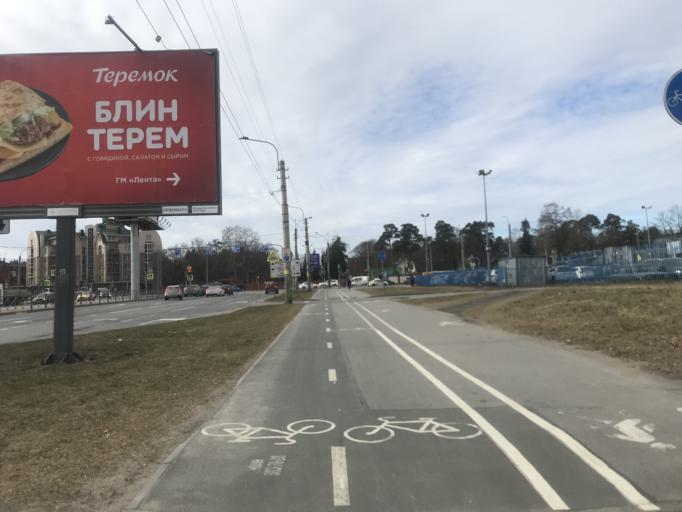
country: RU
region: St.-Petersburg
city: Ozerki
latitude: 60.0443
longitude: 30.3173
